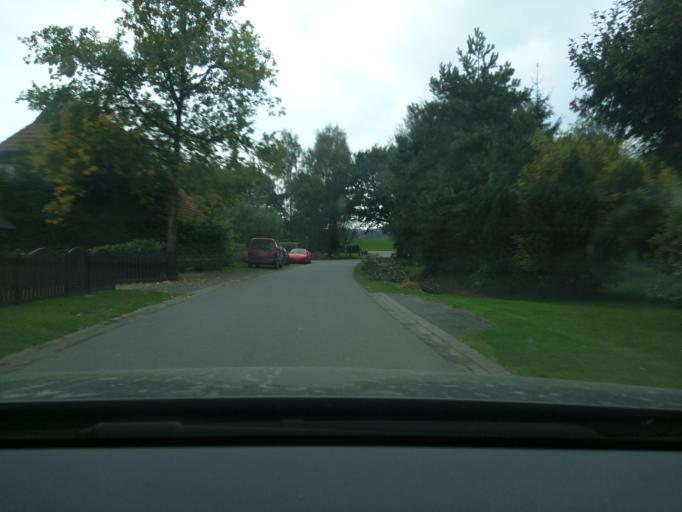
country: DE
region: Lower Saxony
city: Artlenburg
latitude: 53.3695
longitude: 10.4984
